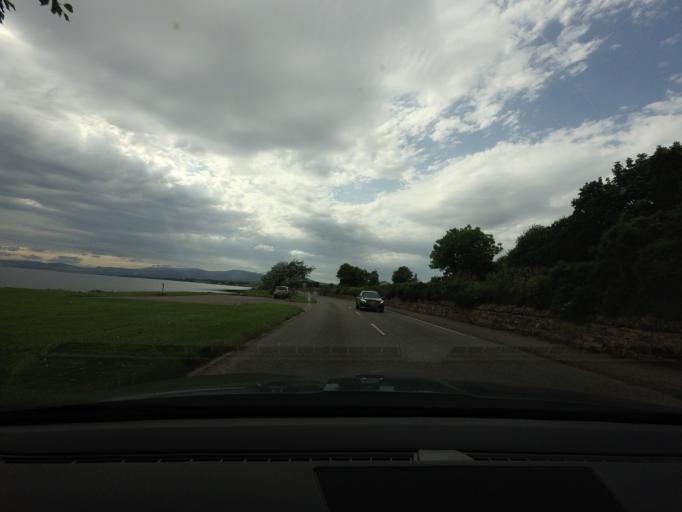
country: GB
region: Scotland
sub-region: Highland
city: Invergordon
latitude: 57.6910
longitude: -4.1874
